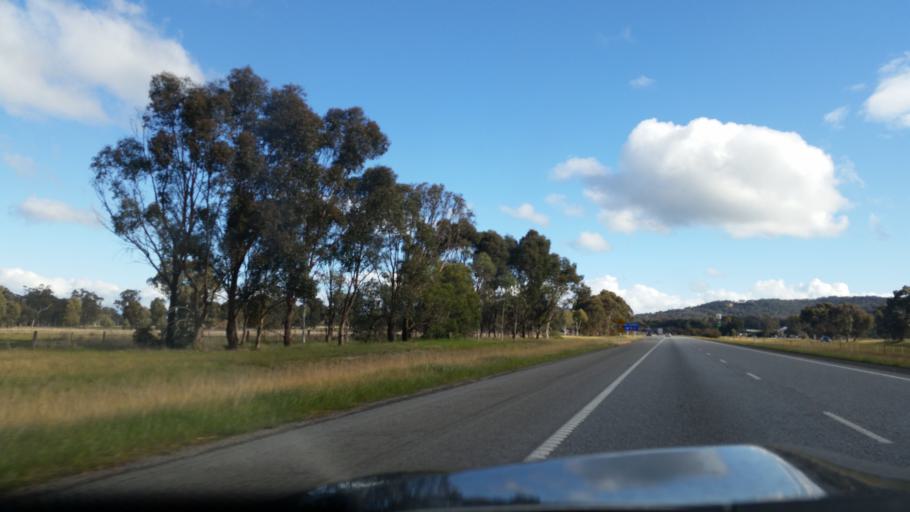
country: AU
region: Victoria
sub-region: Wangaratta
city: Wangaratta
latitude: -36.4348
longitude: 146.2536
